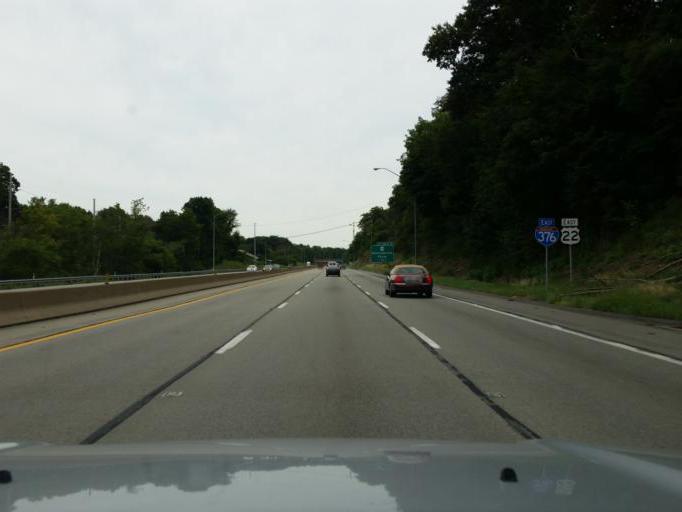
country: US
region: Pennsylvania
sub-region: Allegheny County
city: Monroeville
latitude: 40.4428
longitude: -79.7845
